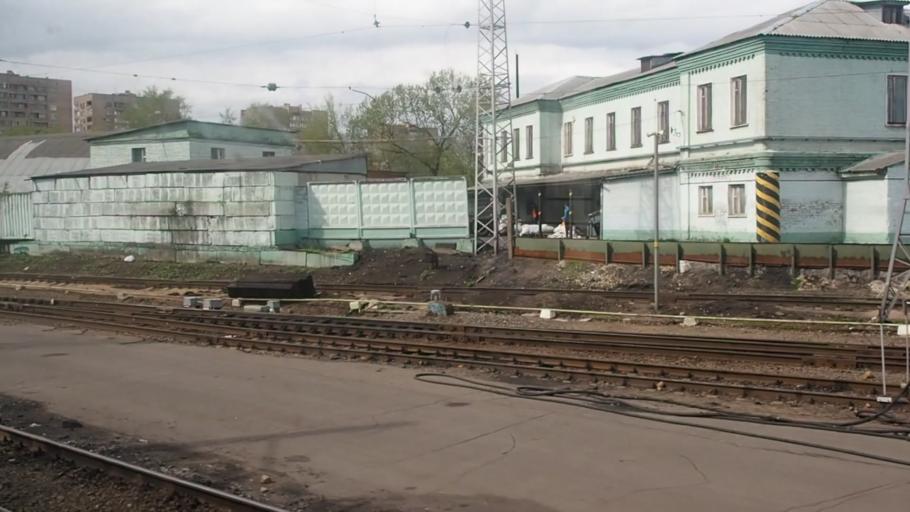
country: RU
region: Moskovskaya
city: Dorogomilovo
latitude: 55.7734
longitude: 37.5622
